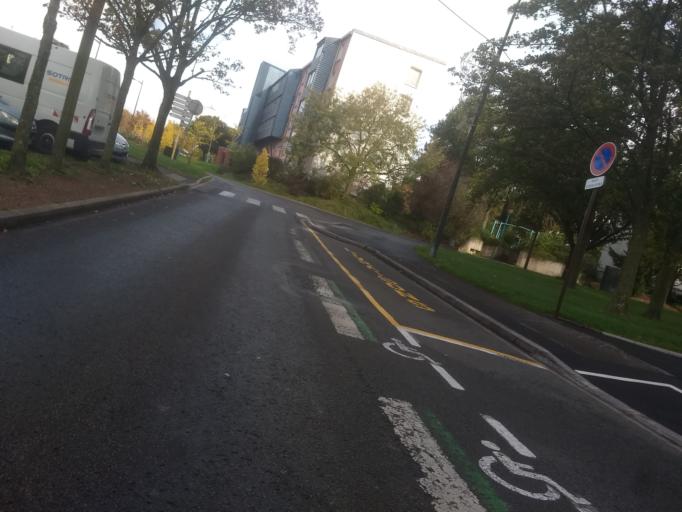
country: FR
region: Nord-Pas-de-Calais
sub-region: Departement du Pas-de-Calais
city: Anzin-Saint-Aubin
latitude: 50.2926
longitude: 2.7479
